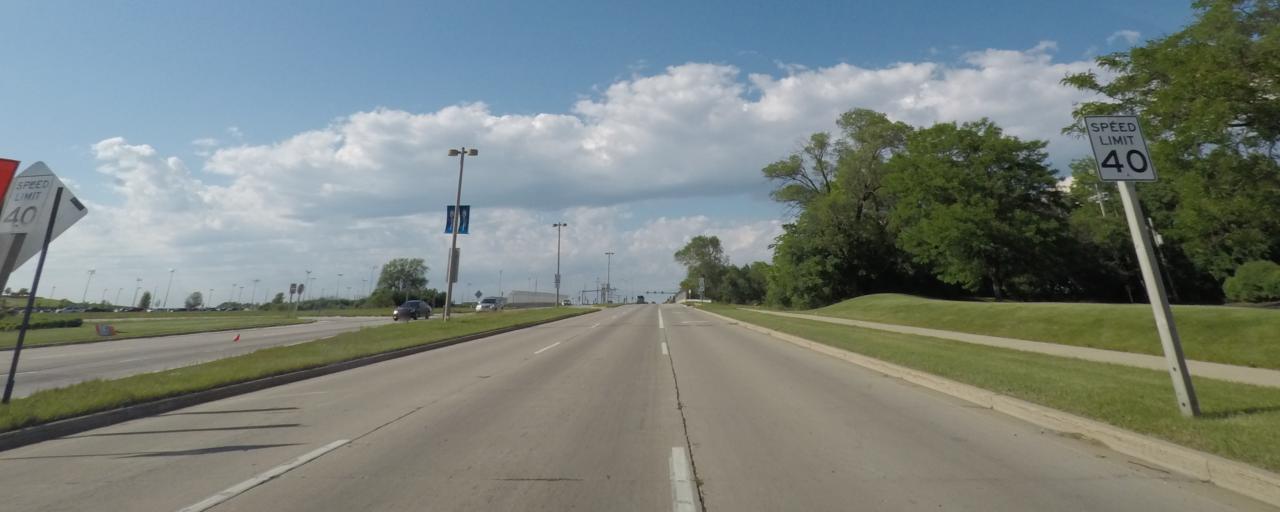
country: US
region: Wisconsin
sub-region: Milwaukee County
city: Greendale
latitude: 42.9171
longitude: -88.0092
